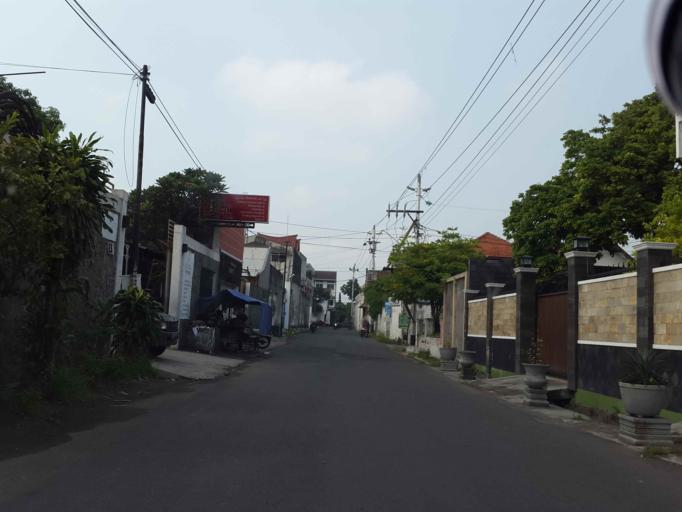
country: ID
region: Central Java
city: Surakarta
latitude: -7.5705
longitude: 110.8132
